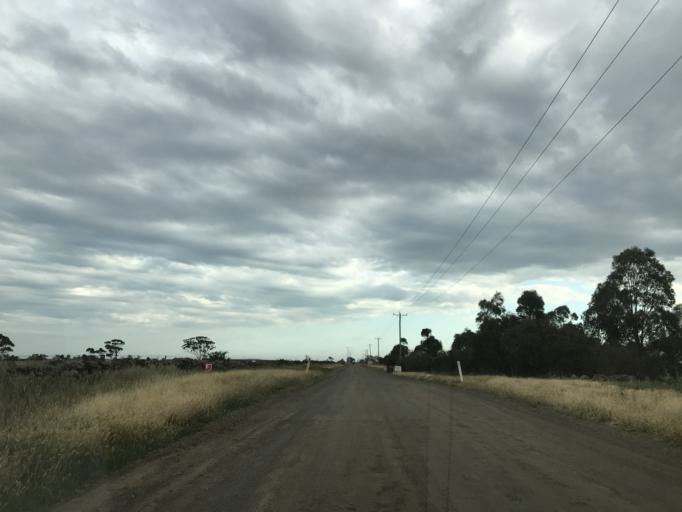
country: AU
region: Victoria
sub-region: Wyndham
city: Truganina
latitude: -37.8102
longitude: 144.7231
